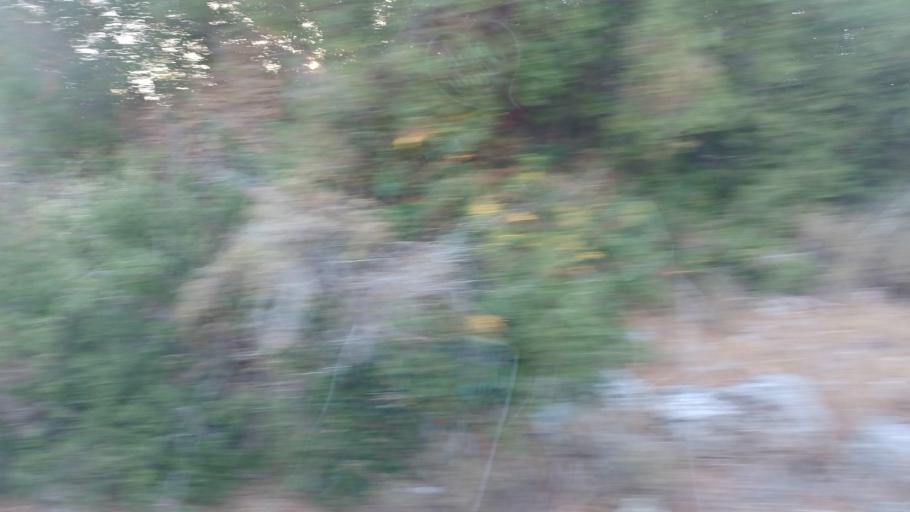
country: CY
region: Pafos
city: Polis
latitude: 34.9752
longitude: 32.4275
